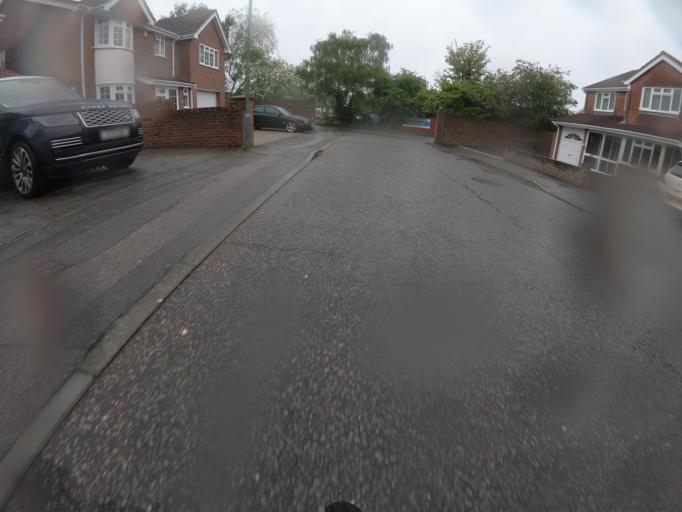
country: GB
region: England
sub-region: Kent
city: Gravesend
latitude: 51.4295
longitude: 0.3475
